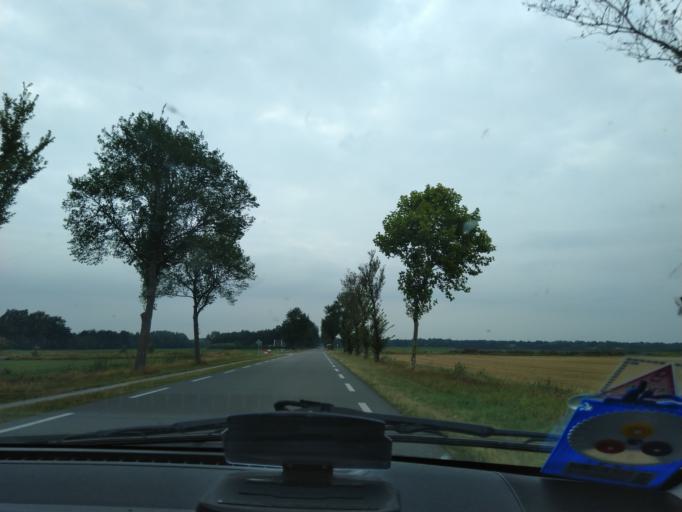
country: NL
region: Groningen
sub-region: Gemeente Vlagtwedde
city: Vlagtwedde
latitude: 53.0810
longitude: 7.1819
